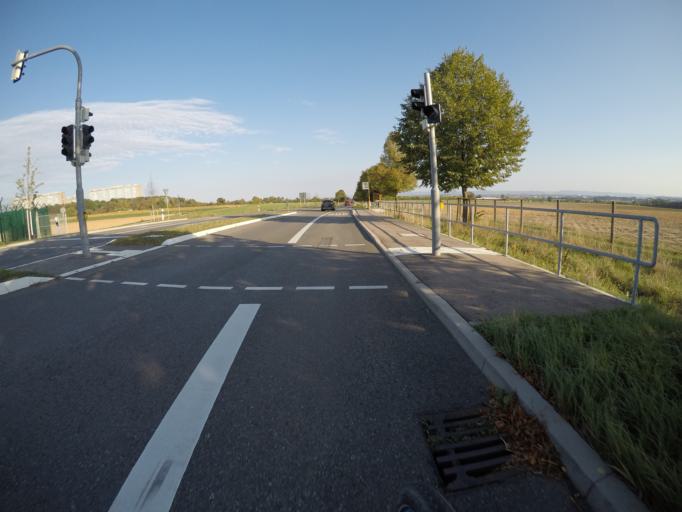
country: DE
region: Baden-Wuerttemberg
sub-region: Regierungsbezirk Stuttgart
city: Leinfelden-Echterdingen
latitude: 48.7212
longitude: 9.1814
